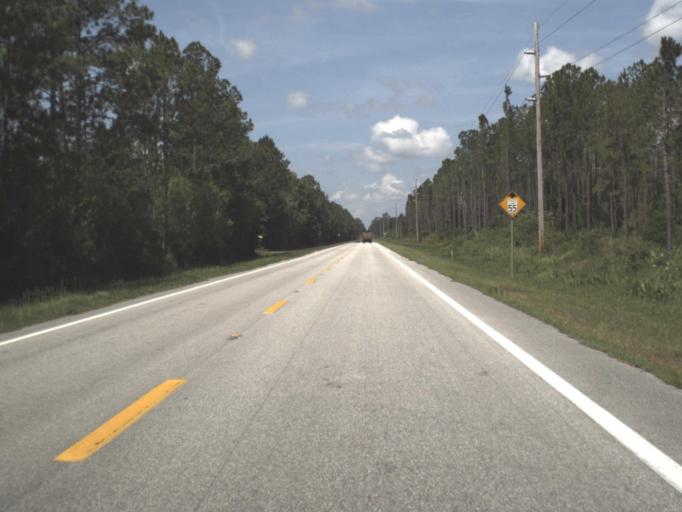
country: US
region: Florida
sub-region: Levy County
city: Bronson
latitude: 29.3337
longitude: -82.7574
